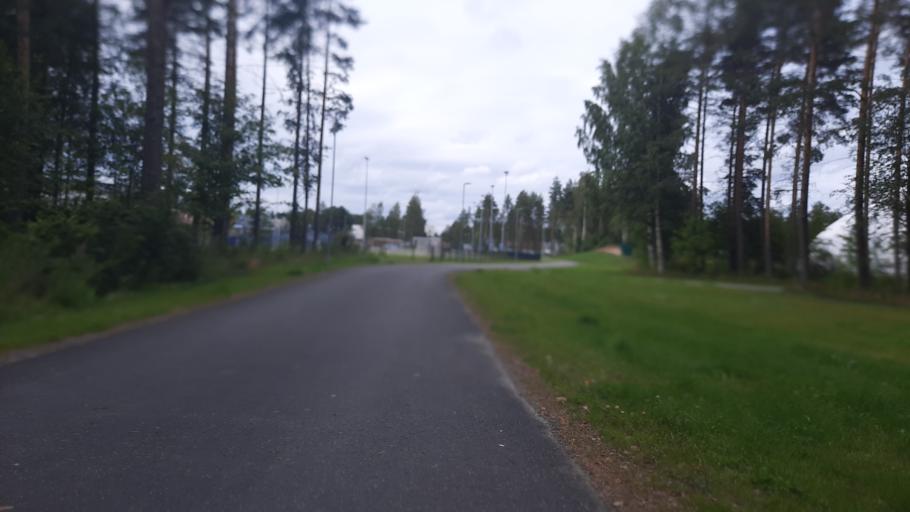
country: FI
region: North Karelia
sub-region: Joensuu
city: Joensuu
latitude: 62.6119
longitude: 29.8236
